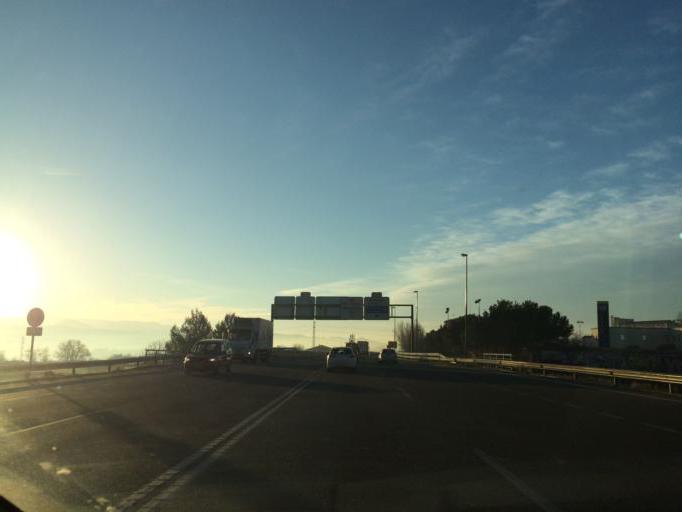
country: ES
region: Catalonia
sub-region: Provincia de Barcelona
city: Sant Fruitos de Bages
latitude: 41.7351
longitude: 1.8504
